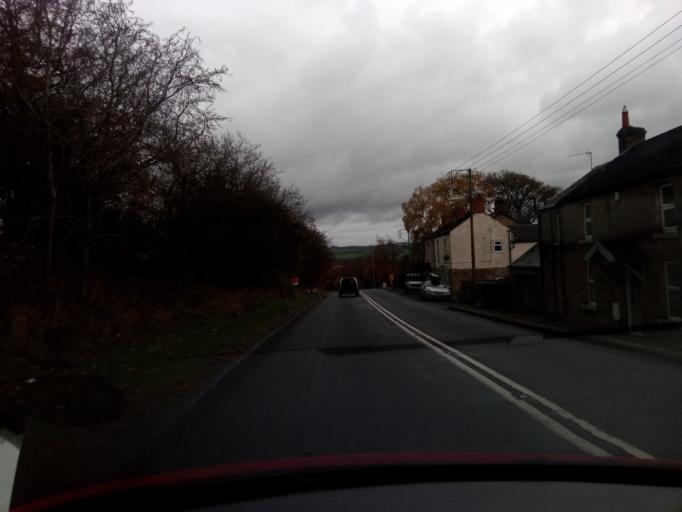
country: GB
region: England
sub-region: County Durham
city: Hamsterley
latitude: 54.6797
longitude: -1.7816
